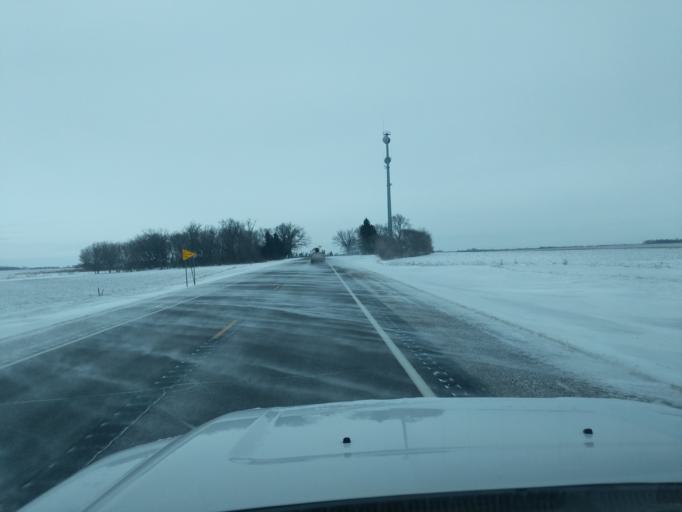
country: US
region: Minnesota
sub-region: Redwood County
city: Redwood Falls
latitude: 44.6005
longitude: -94.9944
